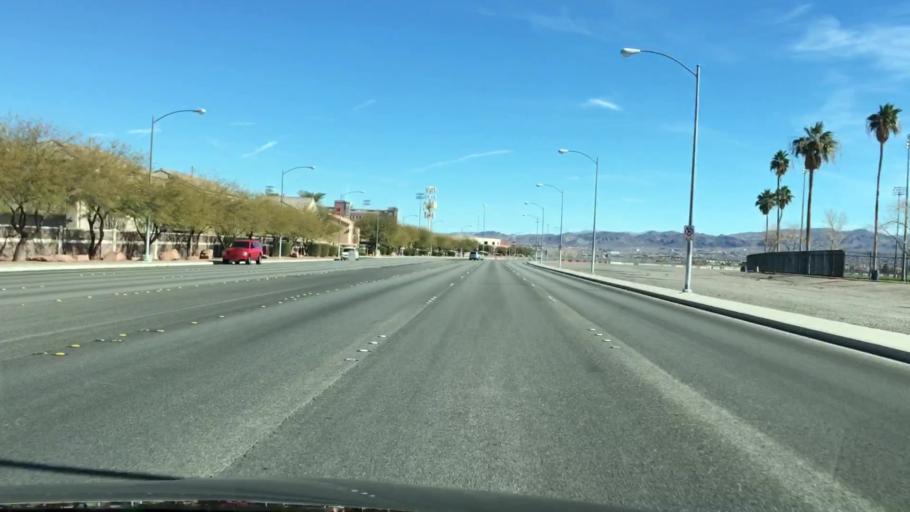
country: US
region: Nevada
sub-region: Clark County
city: Whitney
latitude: 36.0854
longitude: -115.0245
